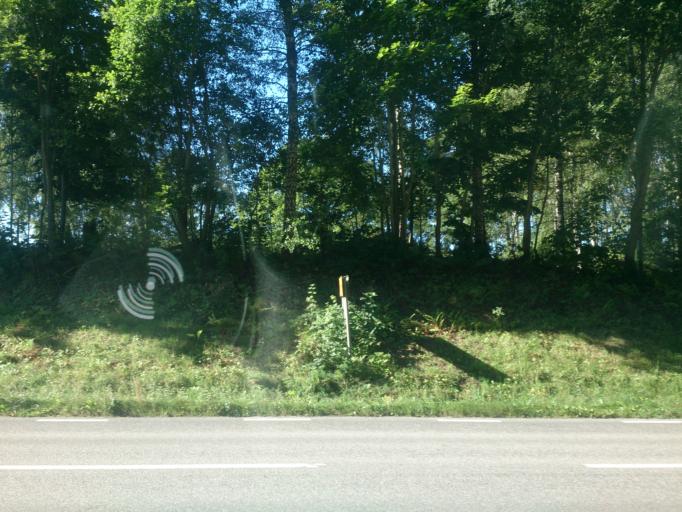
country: SE
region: OEstergoetland
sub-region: Atvidabergs Kommun
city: Atvidaberg
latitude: 58.2713
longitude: 15.9212
